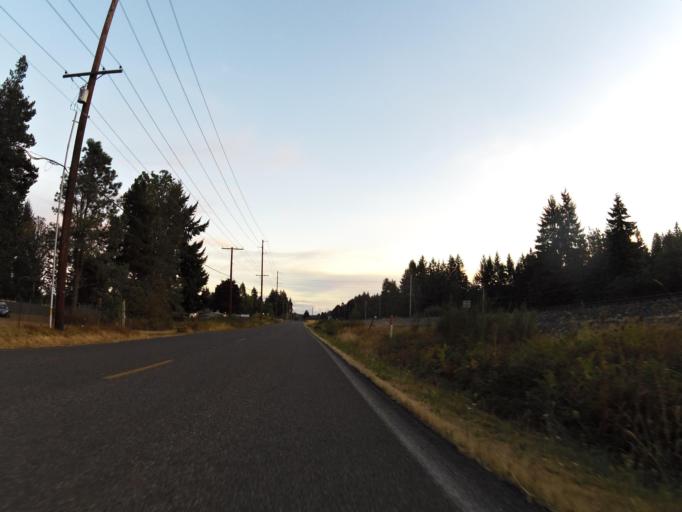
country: US
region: Washington
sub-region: Thurston County
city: Tenino
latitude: 46.8379
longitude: -122.8612
